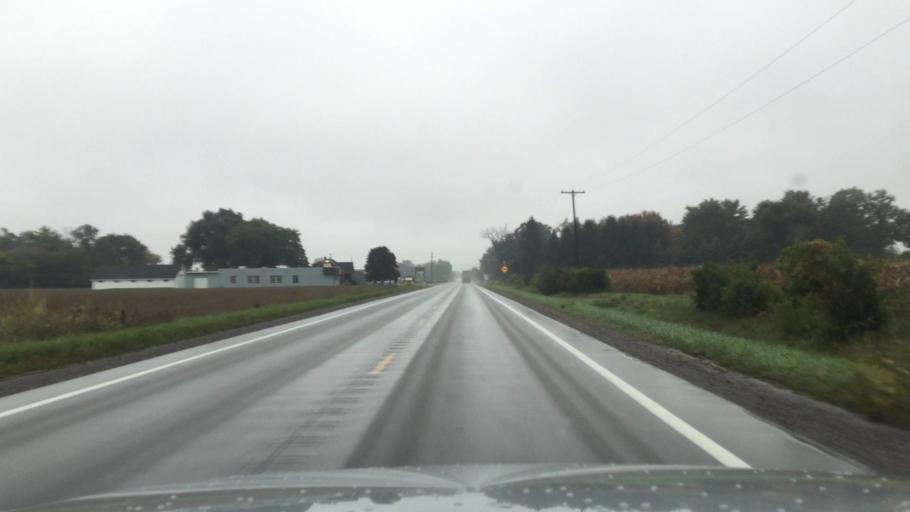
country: US
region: Michigan
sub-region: Saginaw County
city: Saginaw
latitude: 43.3537
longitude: -83.9545
